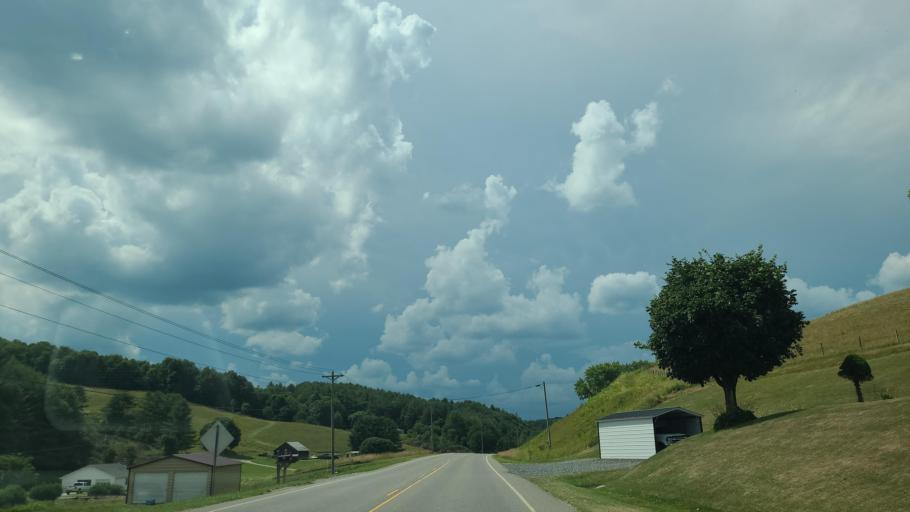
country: US
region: North Carolina
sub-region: Ashe County
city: Jefferson
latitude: 36.3614
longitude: -81.3884
